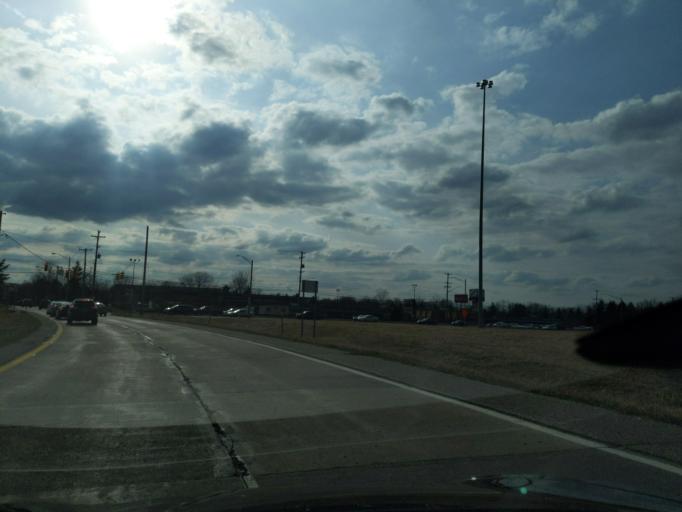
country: US
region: Michigan
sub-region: Ingham County
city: Holt
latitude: 42.6661
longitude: -84.5407
